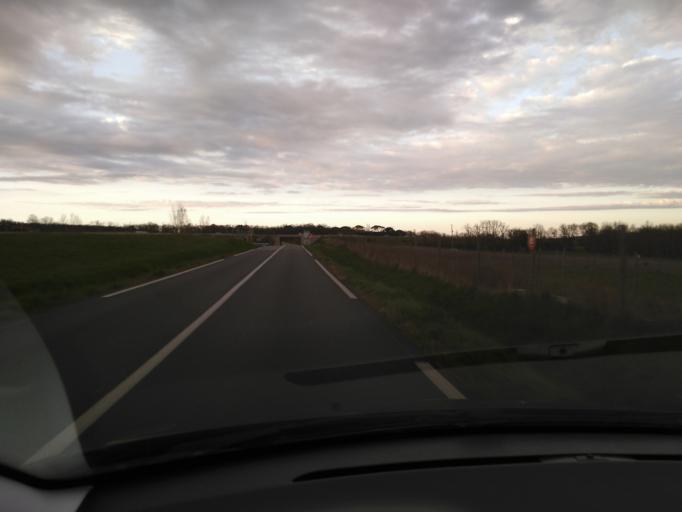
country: FR
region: Midi-Pyrenees
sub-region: Departement de la Haute-Garonne
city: La Salvetat-Saint-Gilles
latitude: 43.5842
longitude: 1.2681
